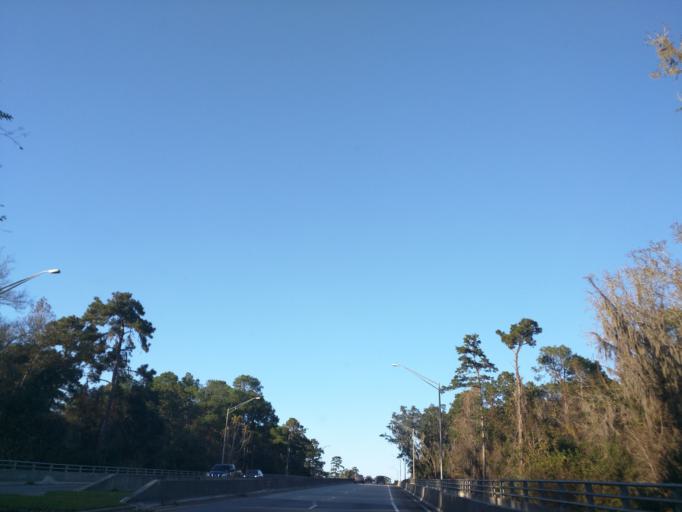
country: US
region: Florida
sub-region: Leon County
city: Tallahassee
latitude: 30.4456
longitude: -84.2506
